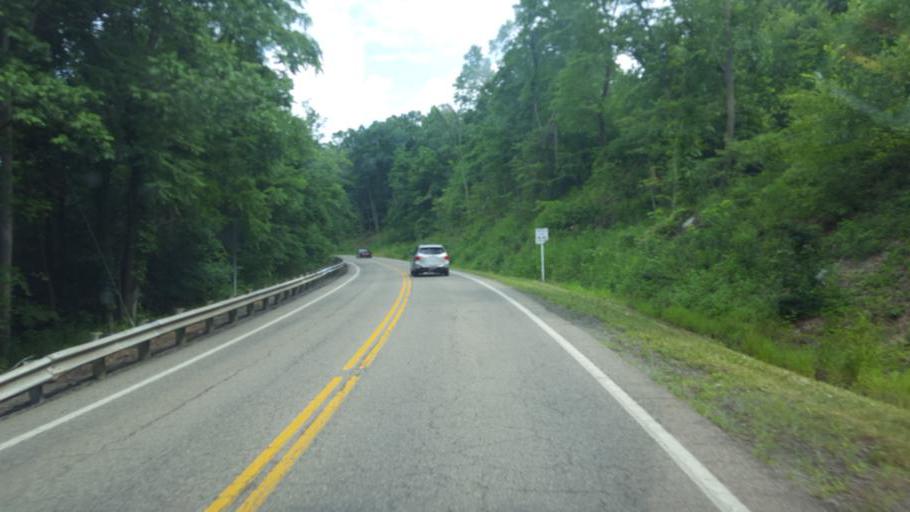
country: US
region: Ohio
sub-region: Columbiana County
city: Lisbon
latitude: 40.7663
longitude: -80.6945
